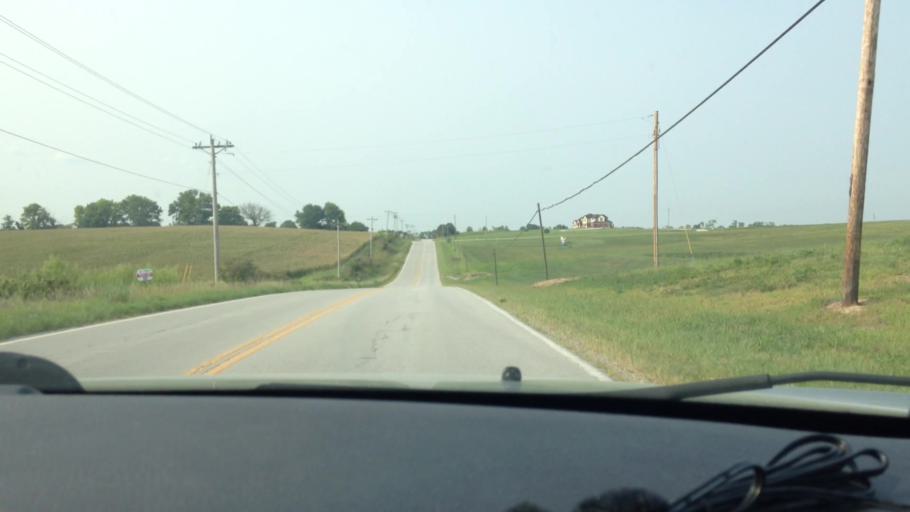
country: US
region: Missouri
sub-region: Platte County
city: Platte City
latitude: 39.4153
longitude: -94.7963
